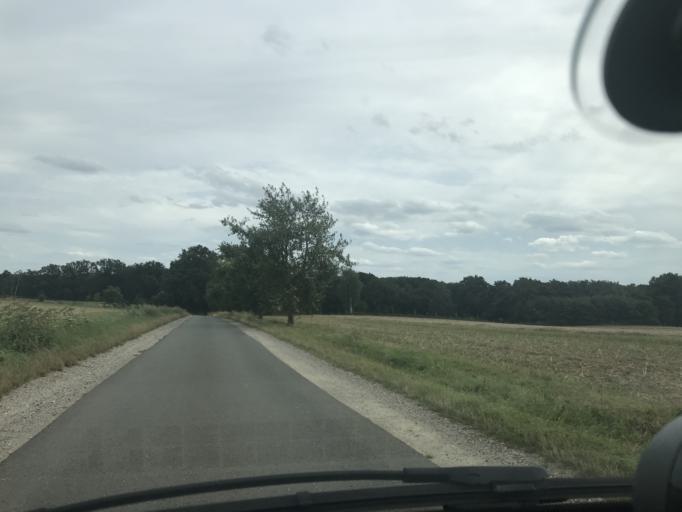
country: DE
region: Lower Saxony
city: Moisburg
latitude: 53.3998
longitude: 9.7187
